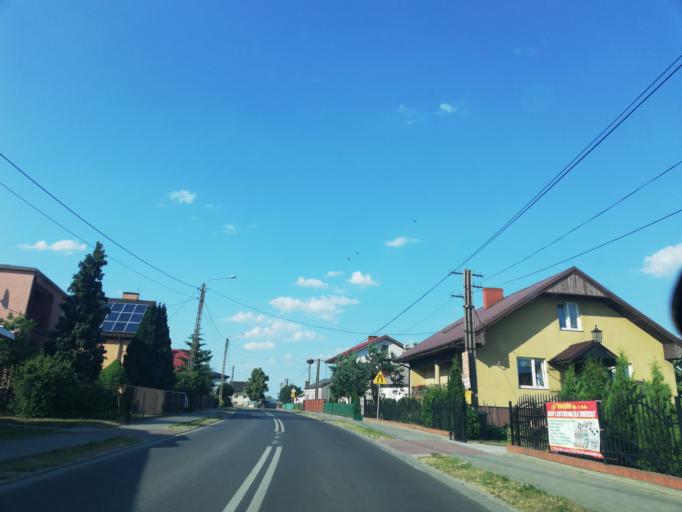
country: PL
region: Kujawsko-Pomorskie
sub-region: Powiat golubsko-dobrzynski
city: Golub-Dobrzyn
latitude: 53.0168
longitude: 19.0569
